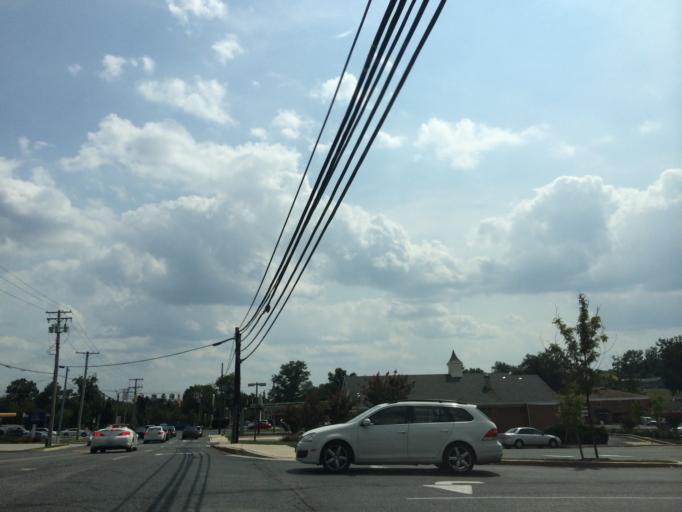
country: US
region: Maryland
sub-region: Howard County
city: Ellicott City
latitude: 39.2781
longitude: -76.8258
